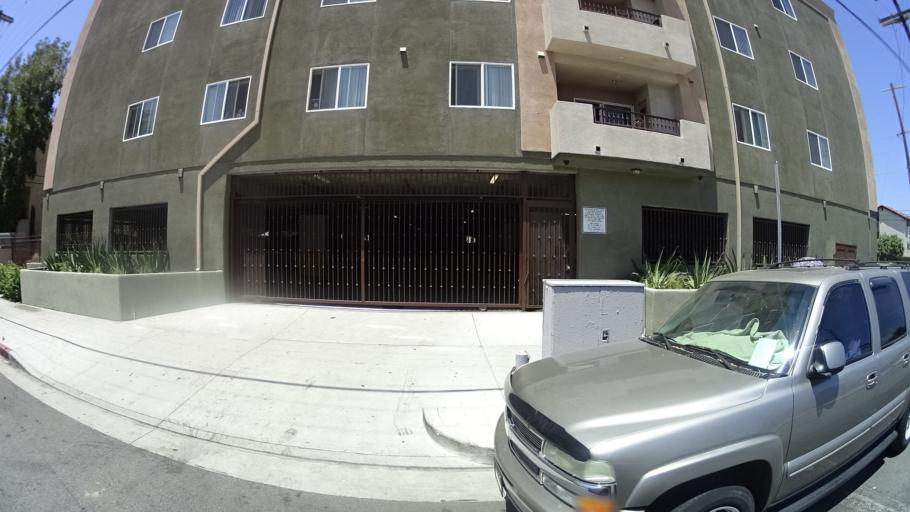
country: US
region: California
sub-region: Los Angeles County
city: Van Nuys
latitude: 34.2350
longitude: -118.4515
